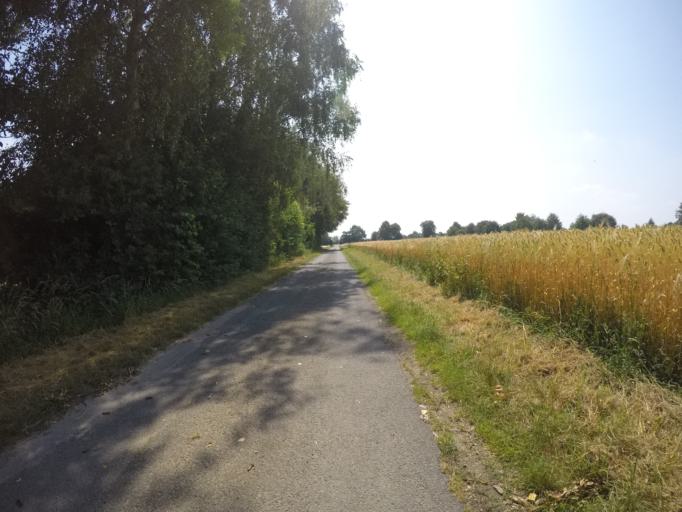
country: DE
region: North Rhine-Westphalia
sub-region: Regierungsbezirk Munster
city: Isselburg
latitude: 51.8285
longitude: 6.5256
